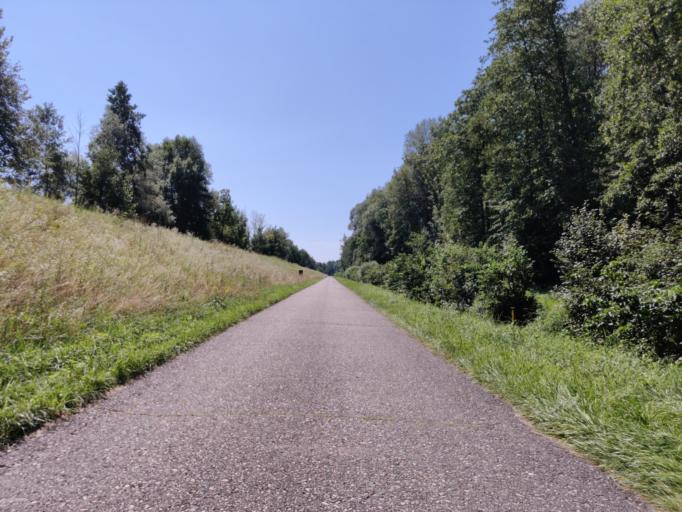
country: AT
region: Styria
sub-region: Politischer Bezirk Leibnitz
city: Gabersdorf
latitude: 46.7928
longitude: 15.5838
